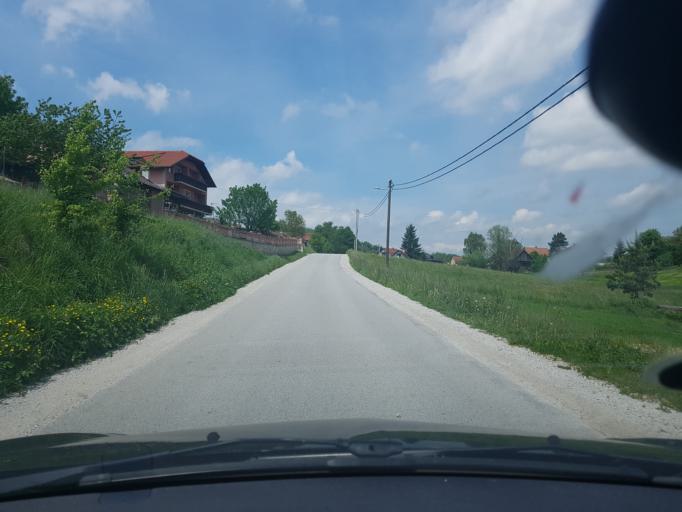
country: SI
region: Rogatec
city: Rogatec
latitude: 46.2057
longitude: 15.7305
